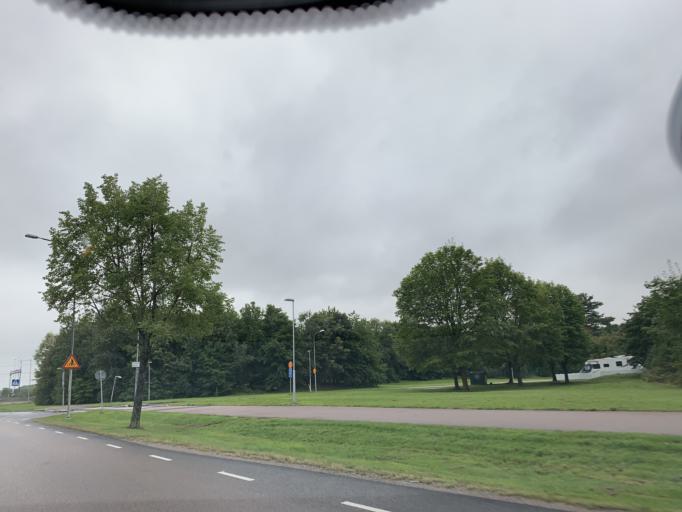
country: SE
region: Vaestmanland
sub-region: Vasteras
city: Vasteras
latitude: 59.5947
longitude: 16.4900
